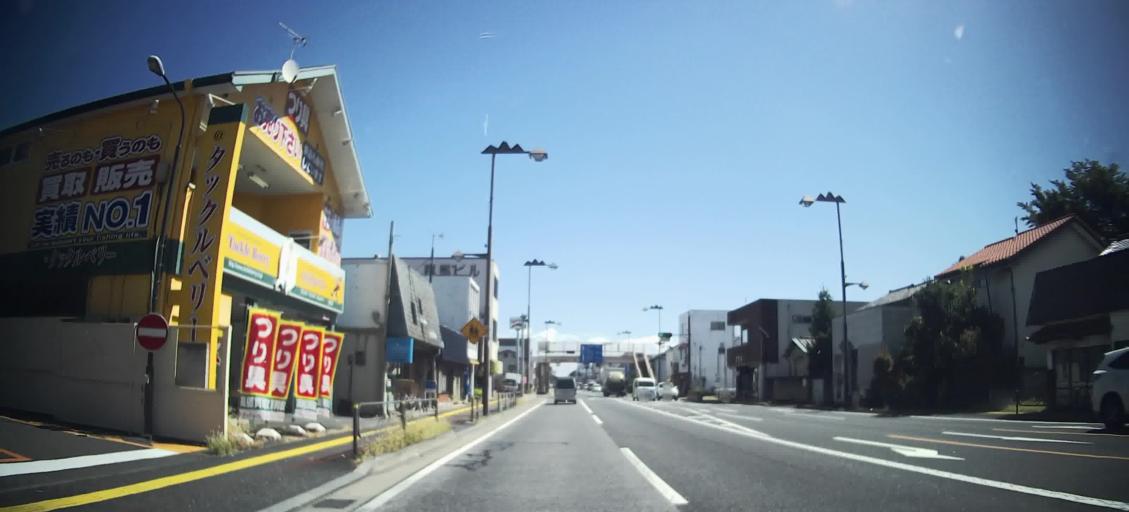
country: JP
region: Gunma
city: Maebashi-shi
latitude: 36.3845
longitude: 139.0850
